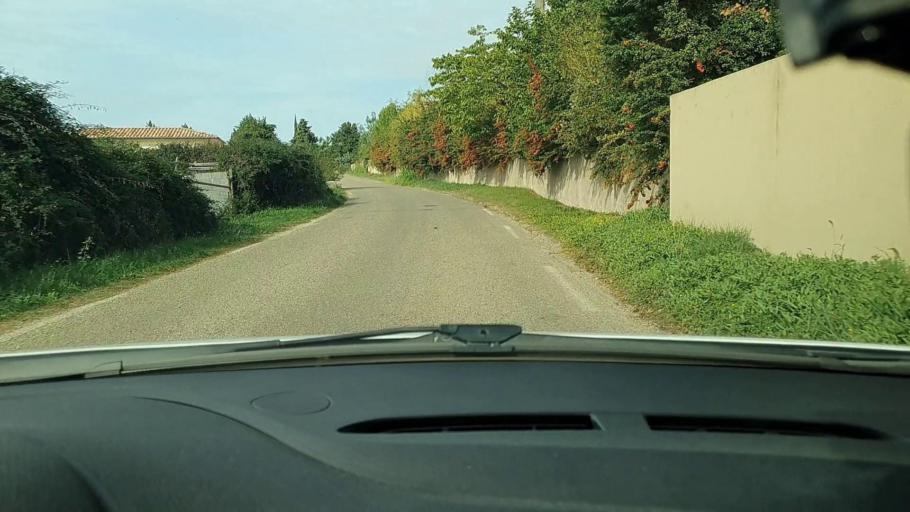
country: FR
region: Languedoc-Roussillon
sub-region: Departement du Gard
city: Saint-Quentin-la-Poterie
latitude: 44.1095
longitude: 4.4189
